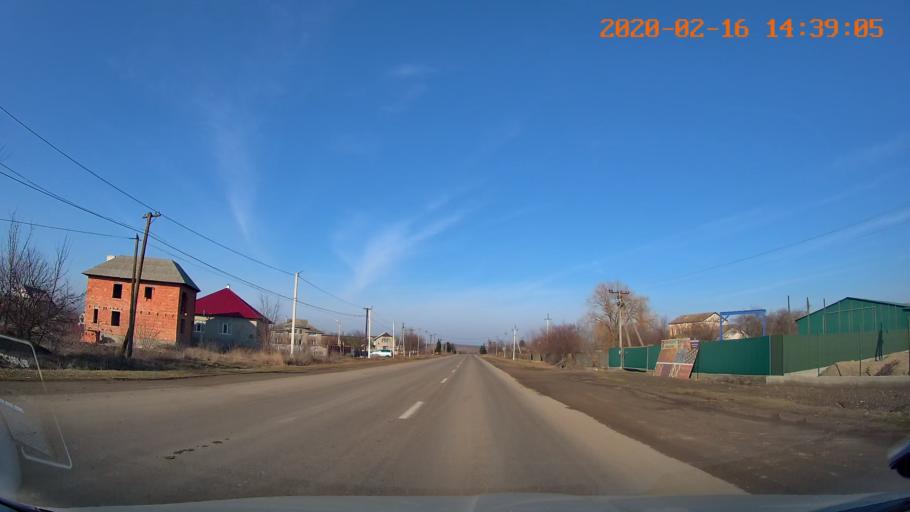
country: RO
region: Botosani
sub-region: Comuna Darabani
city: Bajura
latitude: 48.2384
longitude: 26.5472
